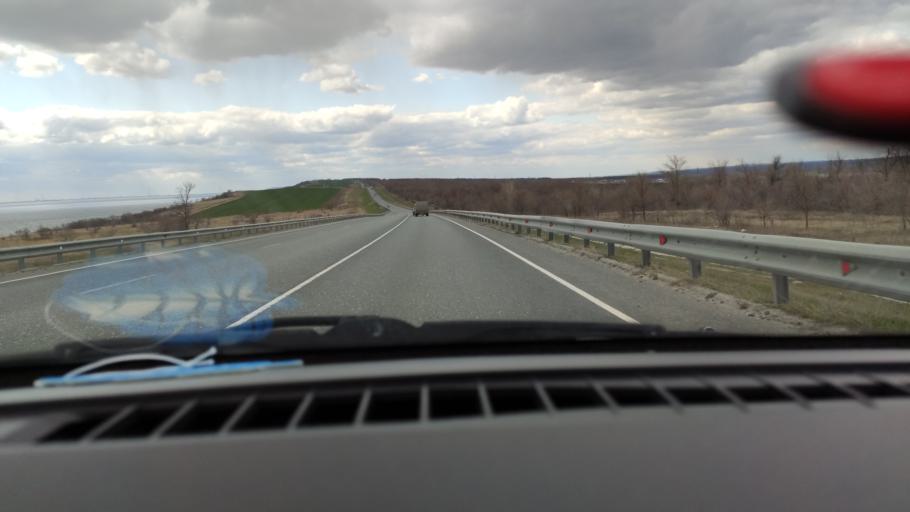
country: RU
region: Saratov
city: Balakovo
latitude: 52.1980
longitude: 47.8611
